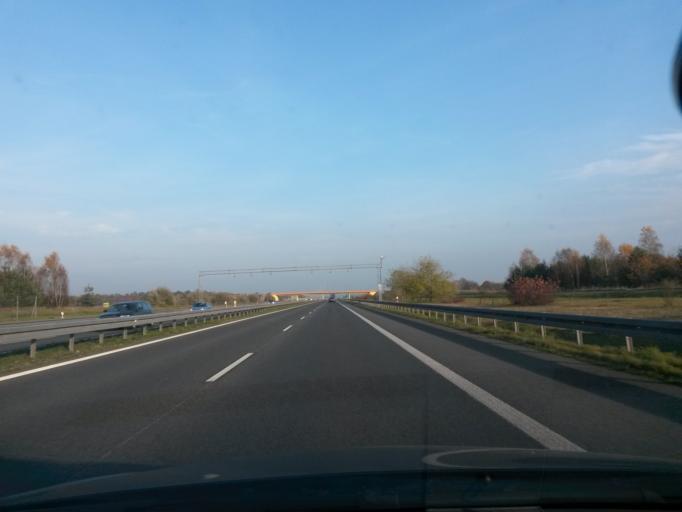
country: PL
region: Lower Silesian Voivodeship
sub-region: Powiat olesnicki
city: Olesnica
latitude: 51.2278
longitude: 17.4618
